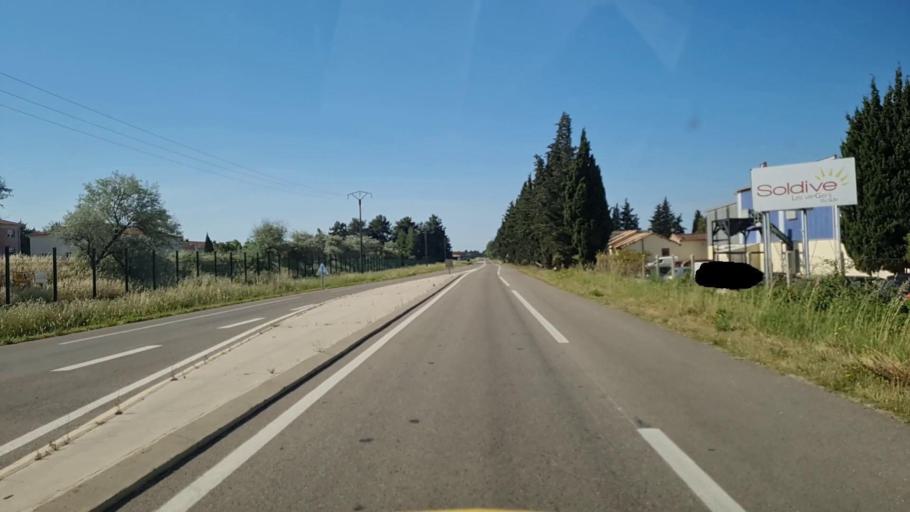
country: FR
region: Languedoc-Roussillon
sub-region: Departement du Gard
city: Garons
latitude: 43.7643
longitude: 4.4056
